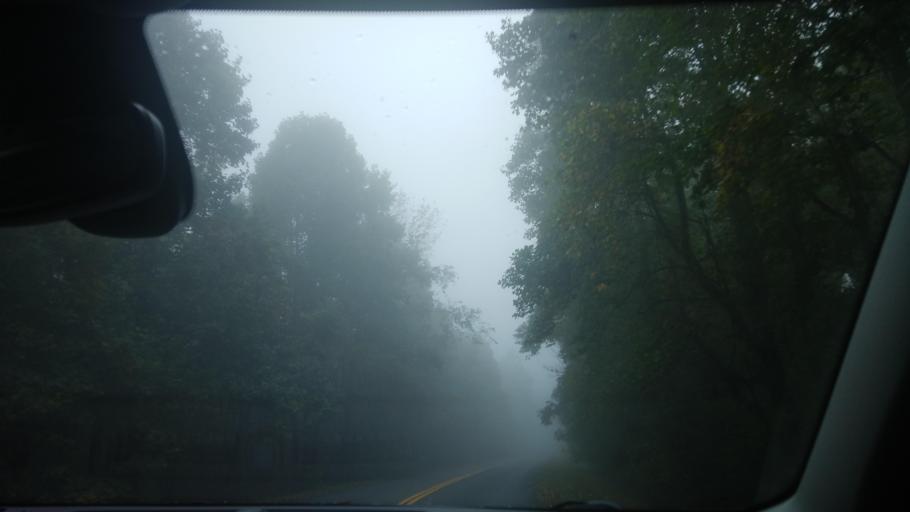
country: US
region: North Carolina
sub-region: Mitchell County
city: Spruce Pine
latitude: 35.8819
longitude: -81.9852
